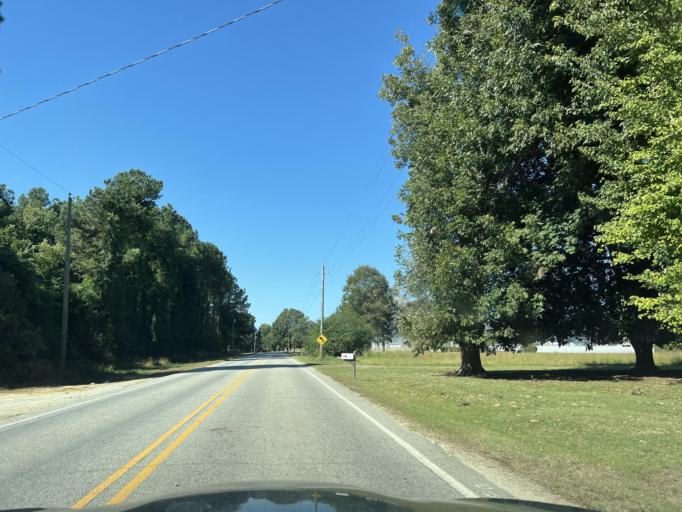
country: US
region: North Carolina
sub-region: Johnston County
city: Clayton
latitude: 35.6709
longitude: -78.4798
